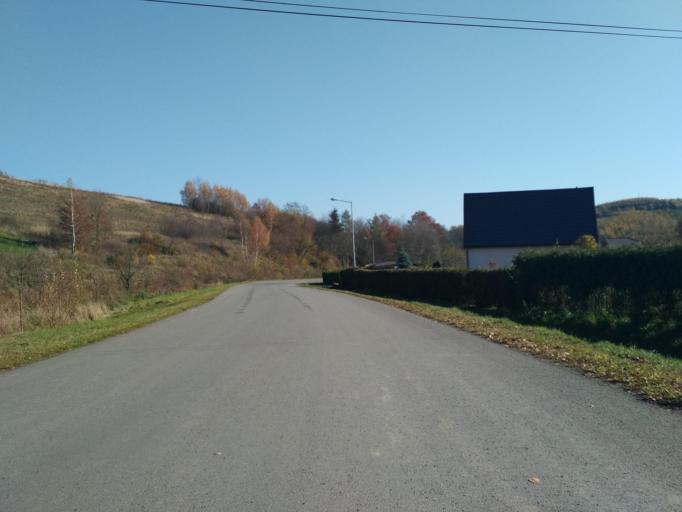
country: PL
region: Subcarpathian Voivodeship
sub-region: Powiat brzozowski
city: Nozdrzec
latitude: 49.7940
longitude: 22.1813
